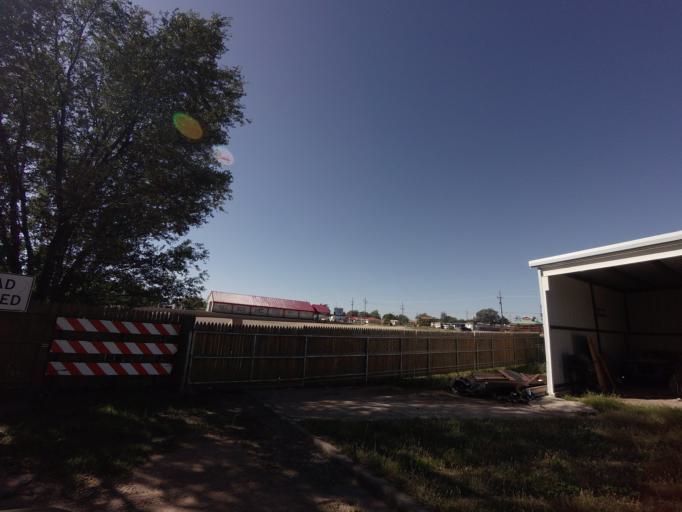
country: US
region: New Mexico
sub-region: Curry County
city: Clovis
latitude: 34.4311
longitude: -103.1953
